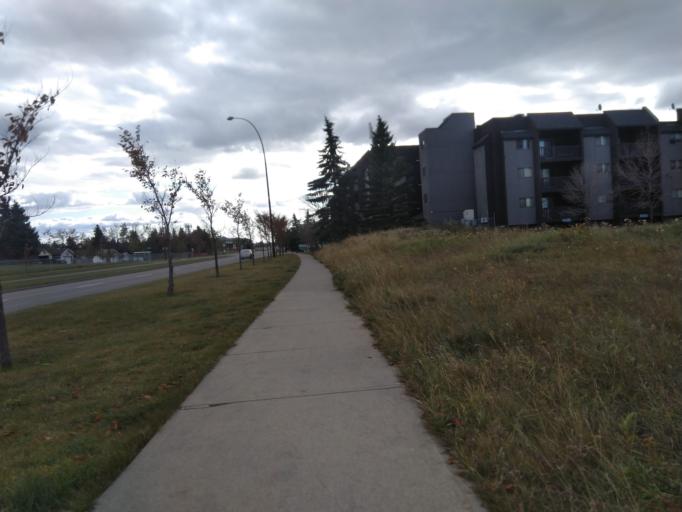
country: CA
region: Alberta
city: Calgary
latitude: 51.0223
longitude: -113.9994
